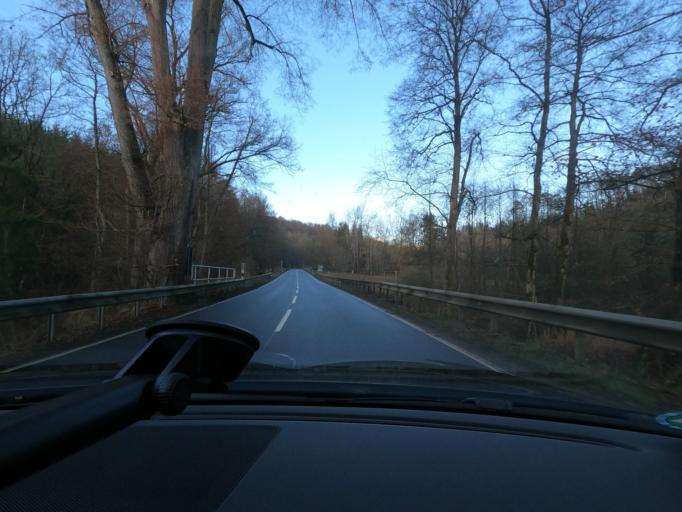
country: DE
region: Lower Saxony
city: Rhumspringe
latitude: 51.5960
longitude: 10.3155
